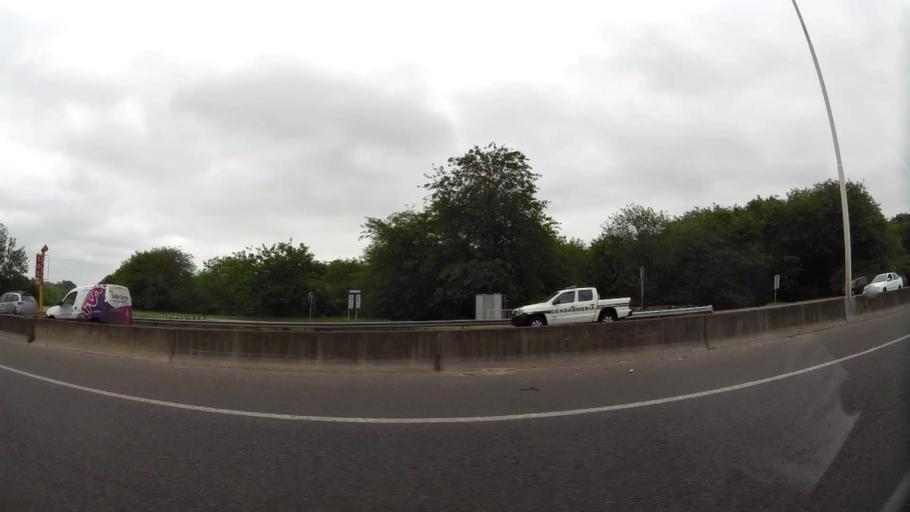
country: AR
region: Buenos Aires
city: San Justo
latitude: -34.7507
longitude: -58.5226
